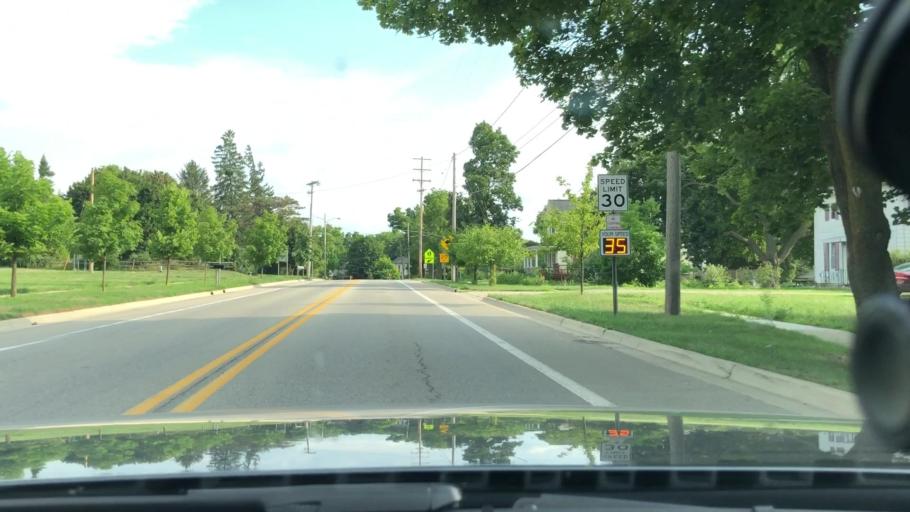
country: US
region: Michigan
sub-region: Washtenaw County
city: Manchester
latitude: 42.1550
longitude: -84.0410
